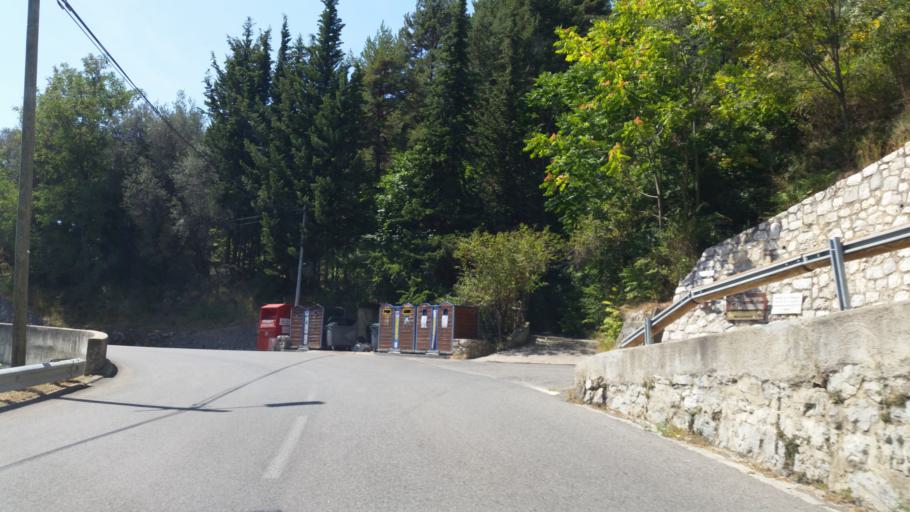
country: FR
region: Provence-Alpes-Cote d'Azur
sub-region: Departement des Alpes-Maritimes
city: Breil-sur-Roya
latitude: 43.9489
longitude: 7.5126
